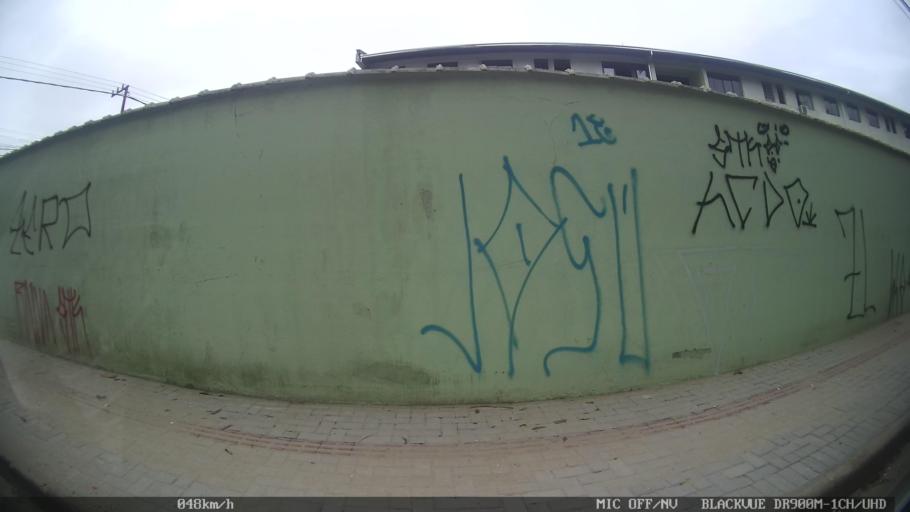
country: BR
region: Santa Catarina
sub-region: Joinville
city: Joinville
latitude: -26.2633
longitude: -48.8515
